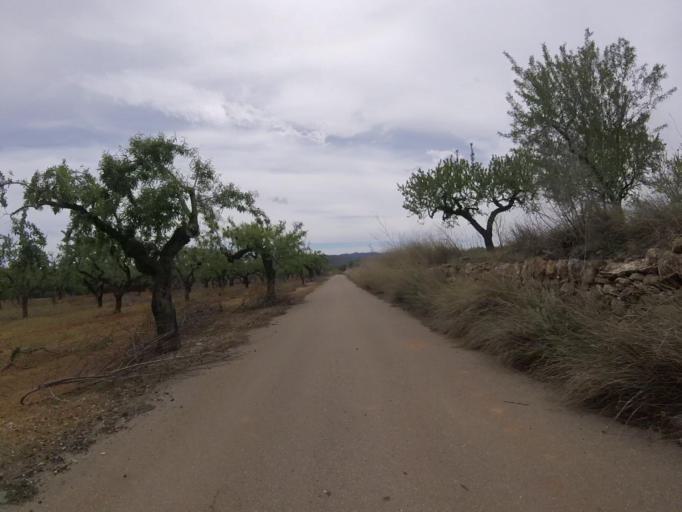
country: ES
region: Valencia
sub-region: Provincia de Castello
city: Benlloch
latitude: 40.1764
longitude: -0.0058
